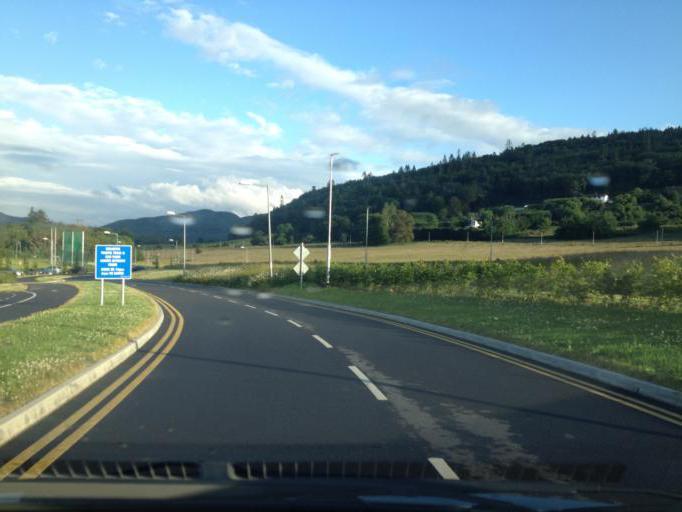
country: IE
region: Connaught
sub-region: Sligo
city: Sligo
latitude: 54.2617
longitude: -8.4492
